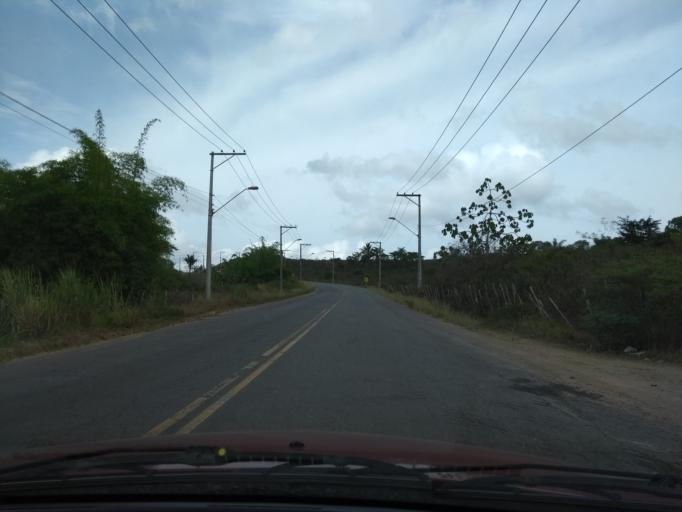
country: BR
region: Bahia
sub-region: Sao Francisco Do Conde
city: Sao Francisco do Conde
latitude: -12.6106
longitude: -38.6516
